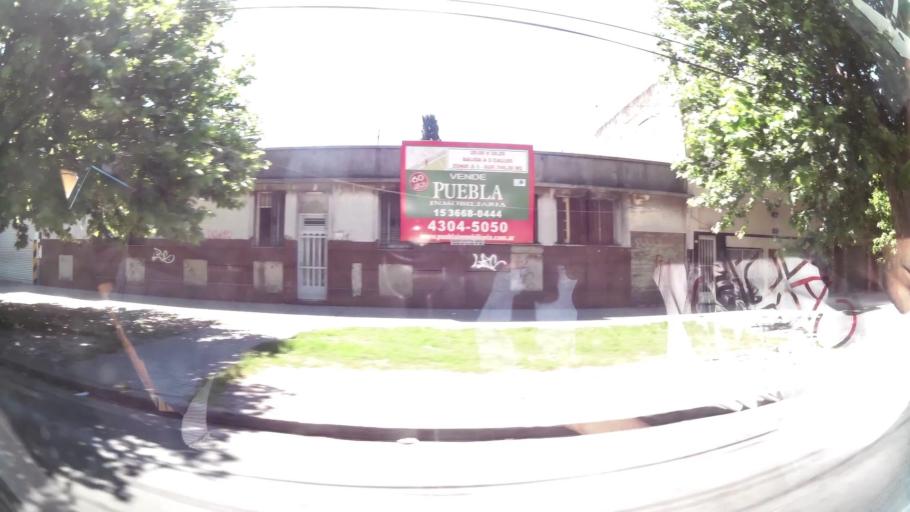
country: AR
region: Buenos Aires F.D.
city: Villa Lugano
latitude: -34.6616
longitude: -58.4332
